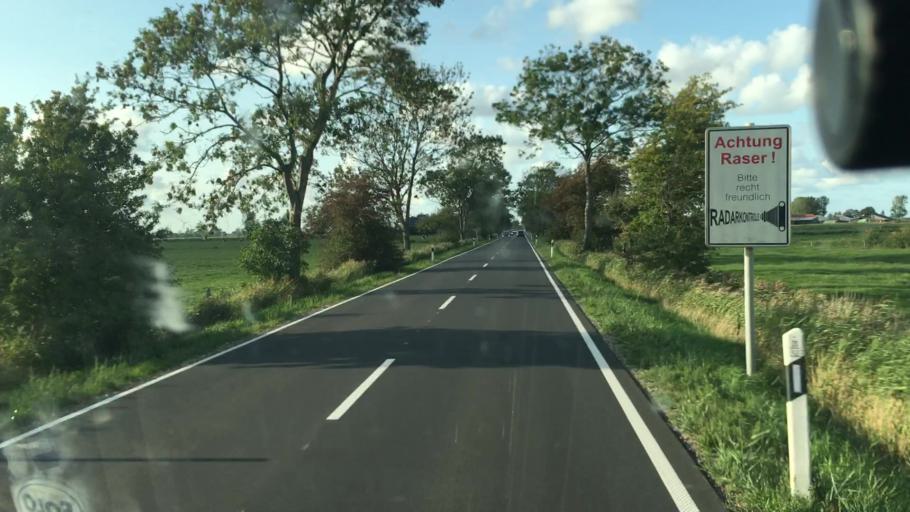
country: DE
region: Lower Saxony
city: Jever
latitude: 53.6175
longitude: 7.8658
